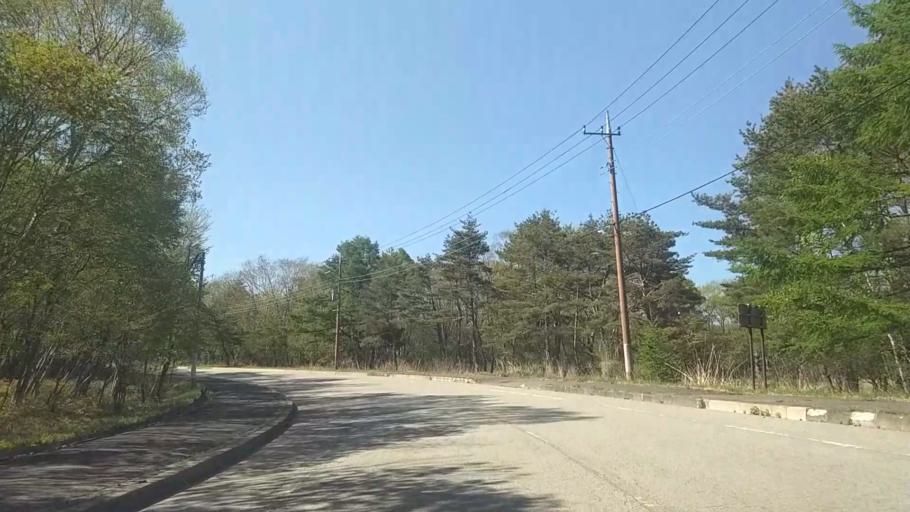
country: JP
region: Yamanashi
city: Nirasaki
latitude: 35.9365
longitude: 138.4426
